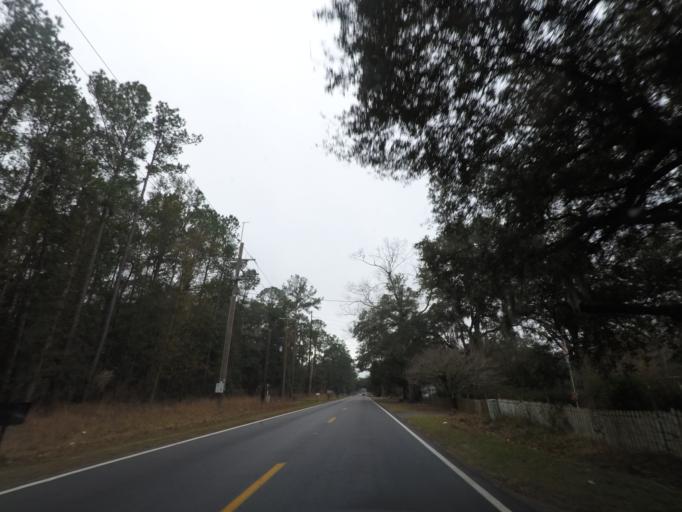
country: US
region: South Carolina
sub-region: Charleston County
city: Hollywood
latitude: 32.7149
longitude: -80.3497
